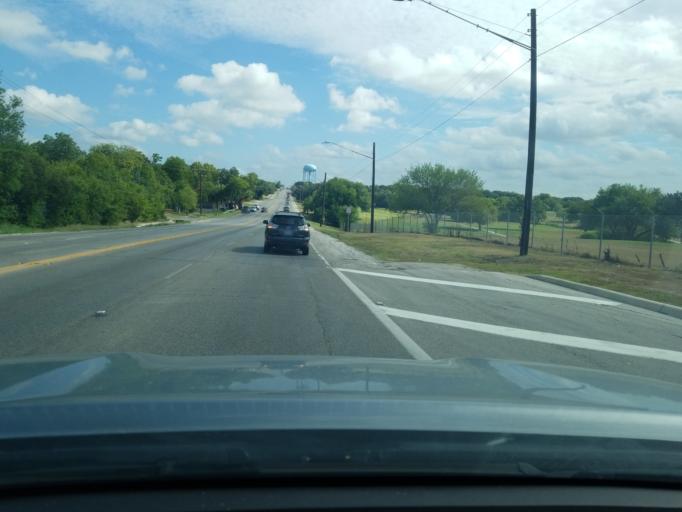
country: US
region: Texas
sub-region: Bexar County
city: Terrell Hills
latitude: 29.4717
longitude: -98.4372
